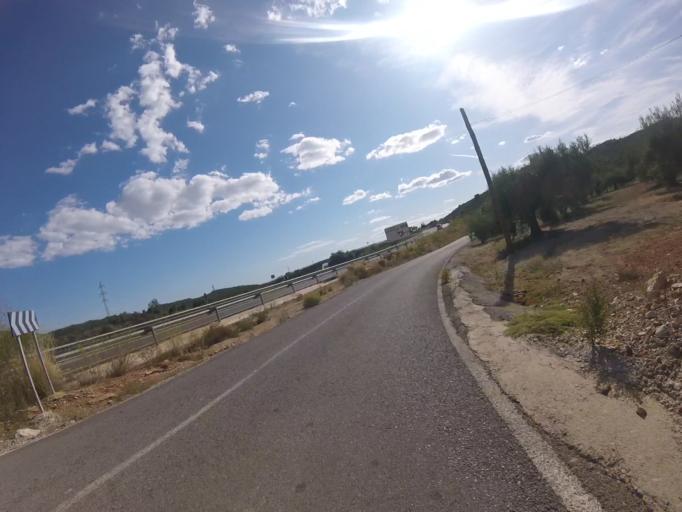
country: ES
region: Valencia
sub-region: Provincia de Castello
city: Alcala de Xivert
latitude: 40.2696
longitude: 0.2403
